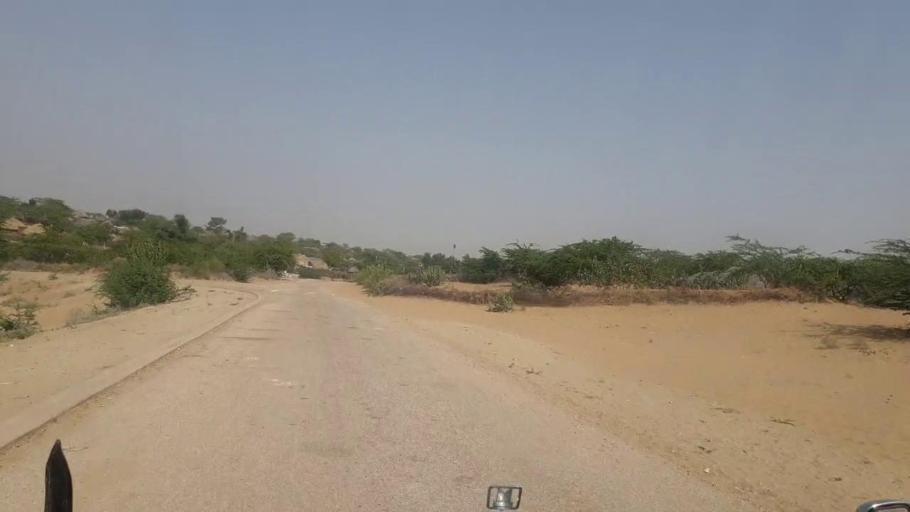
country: PK
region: Sindh
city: Umarkot
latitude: 25.2273
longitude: 70.2452
